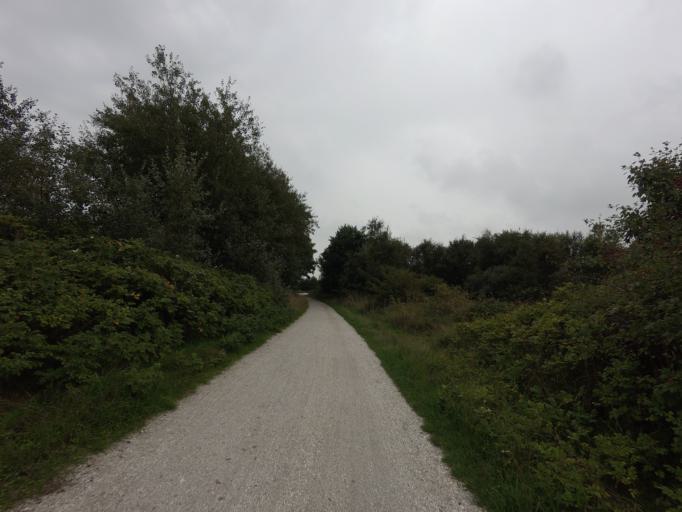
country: NL
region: Friesland
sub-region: Gemeente Schiermonnikoog
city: Schiermonnikoog
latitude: 53.4859
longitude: 6.1594
